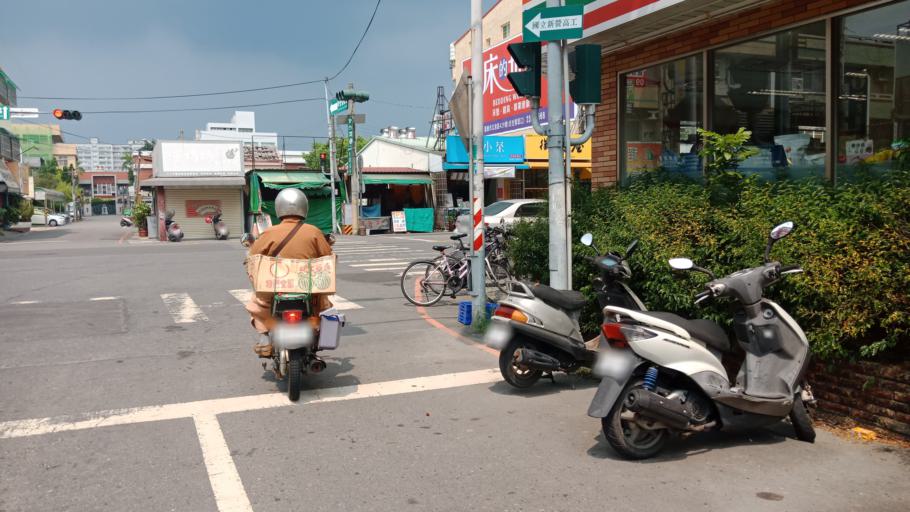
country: TW
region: Taiwan
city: Xinying
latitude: 23.3109
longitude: 120.3226
